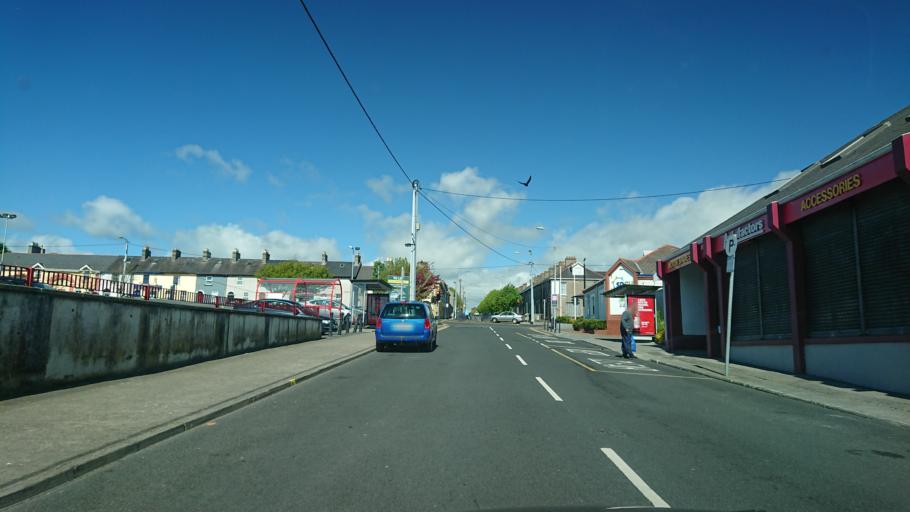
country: IE
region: Munster
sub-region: Waterford
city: Waterford
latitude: 52.2611
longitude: -7.1214
